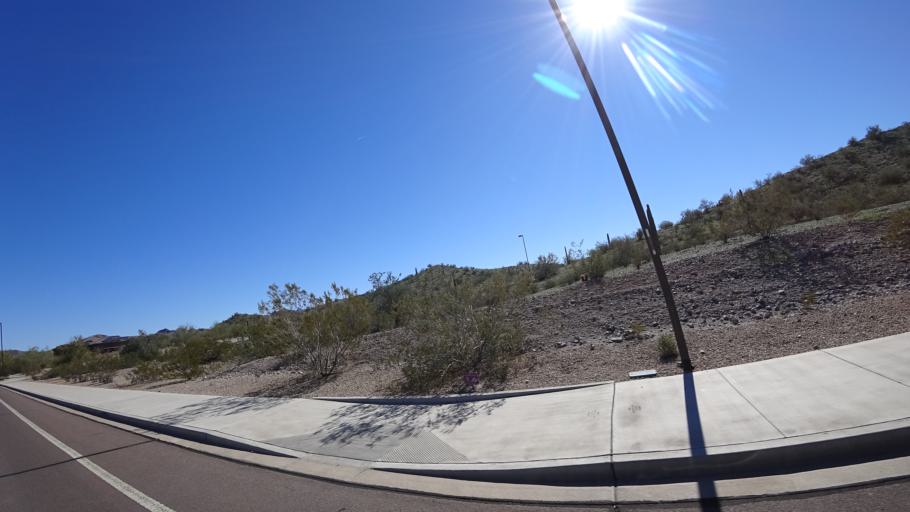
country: US
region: Arizona
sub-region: Maricopa County
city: Goodyear
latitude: 33.3613
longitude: -112.4359
